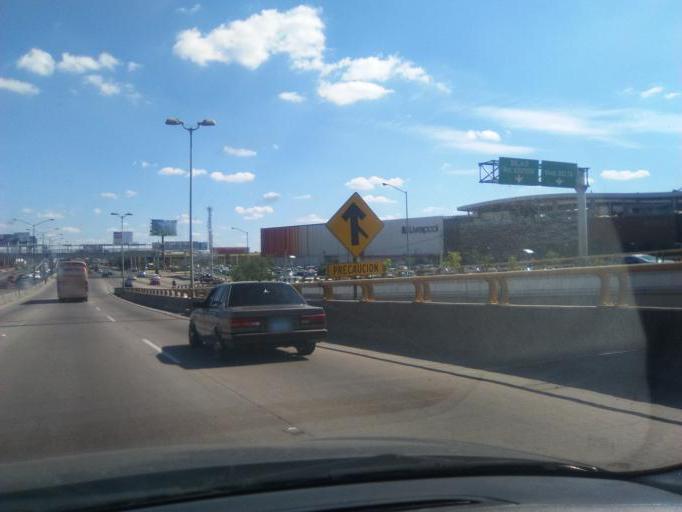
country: MX
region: Guanajuato
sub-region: Leon
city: Fraccionamiento Paraiso Real
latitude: 21.0946
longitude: -101.6259
